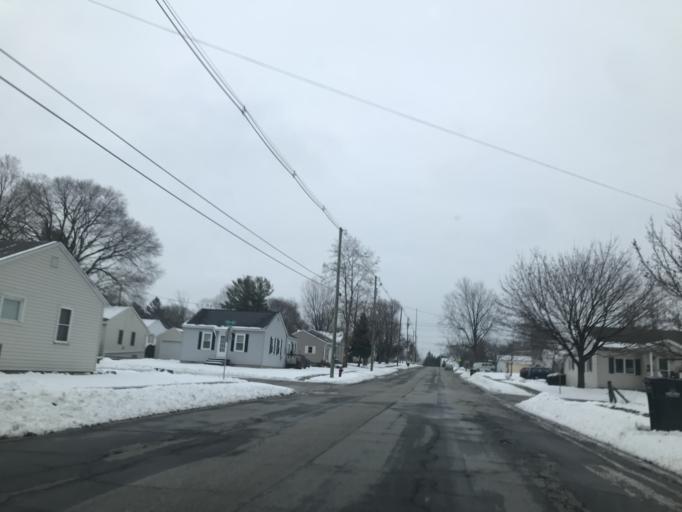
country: US
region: Wisconsin
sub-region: Door County
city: Sturgeon Bay
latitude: 44.8456
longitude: -87.3748
